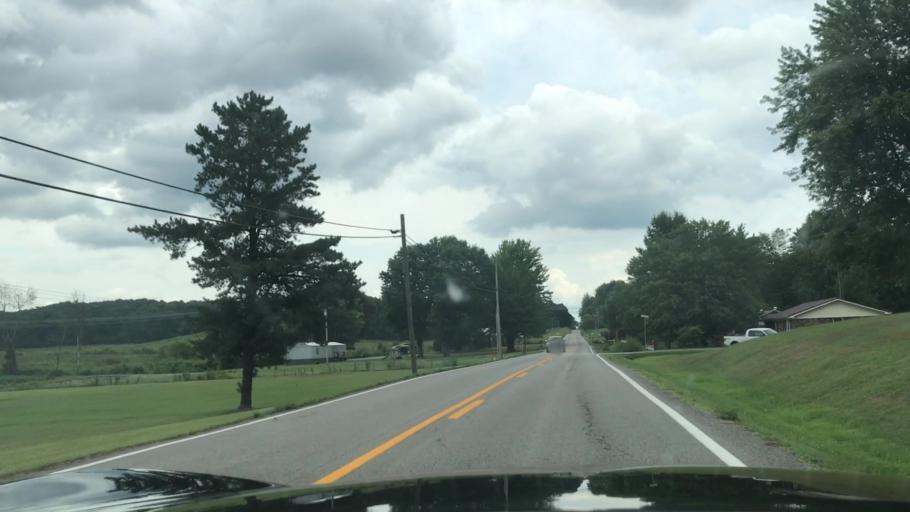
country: US
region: Kentucky
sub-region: Muhlenberg County
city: Central City
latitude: 37.2013
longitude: -87.0074
